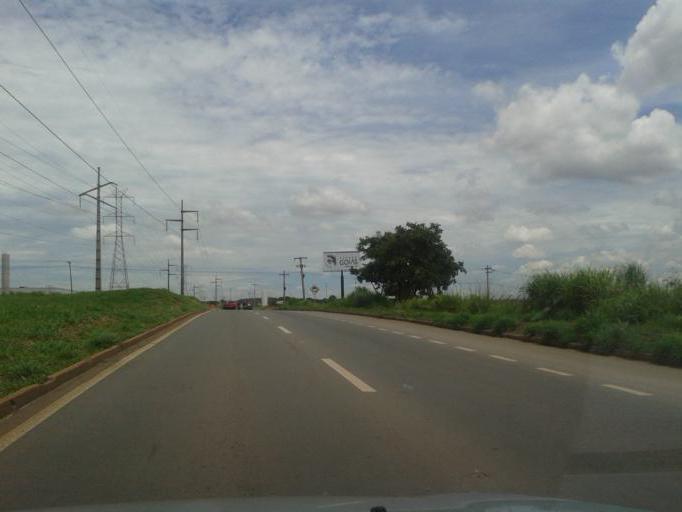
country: BR
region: Goias
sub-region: Aparecida De Goiania
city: Aparecida de Goiania
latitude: -16.7863
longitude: -49.2496
